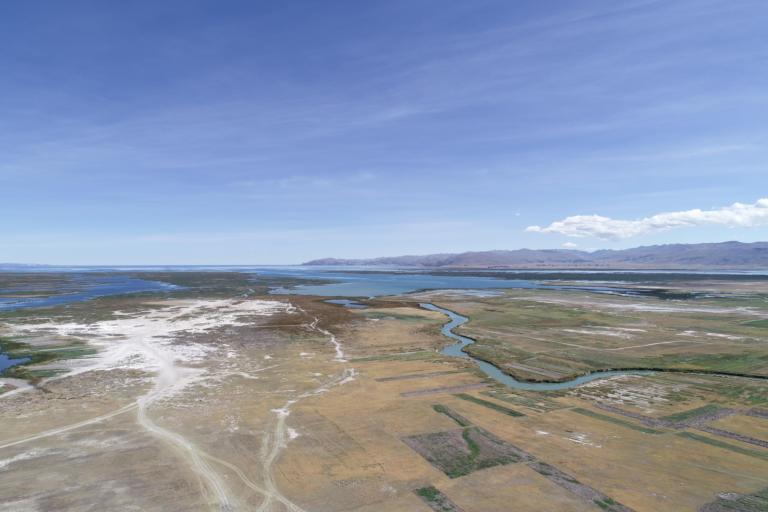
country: BO
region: La Paz
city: Achacachi
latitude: -16.0087
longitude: -68.7344
